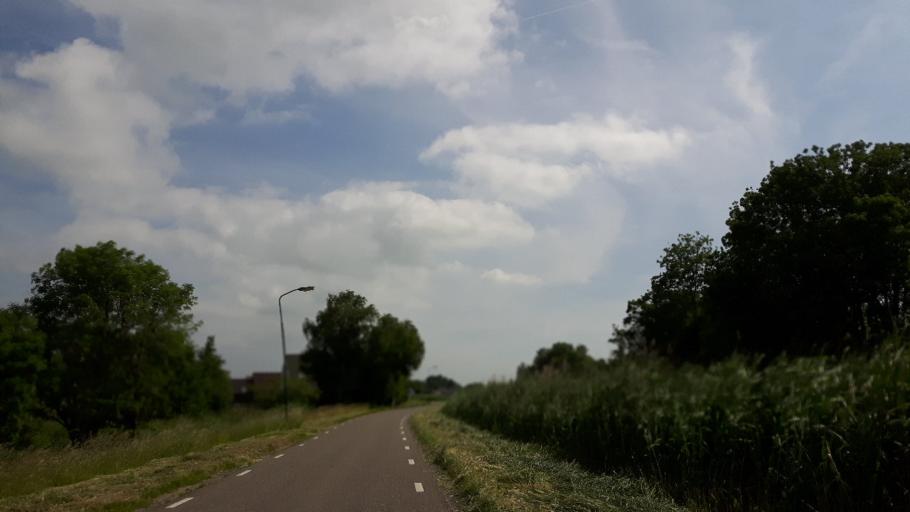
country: NL
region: Utrecht
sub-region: Gemeente De Ronde Venen
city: Mijdrecht
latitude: 52.1683
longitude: 4.8686
